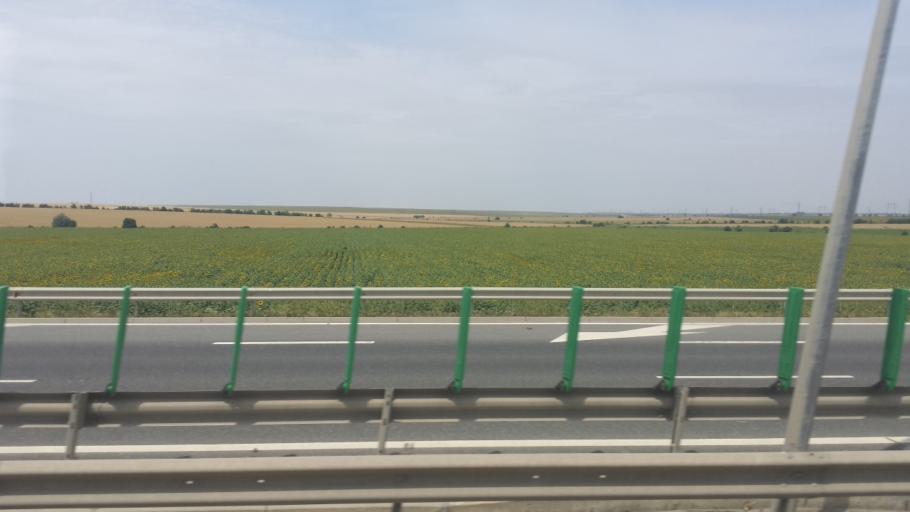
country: RO
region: Constanta
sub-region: Municipiul Constanta
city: Palazu Mare
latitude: 44.2080
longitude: 28.5531
